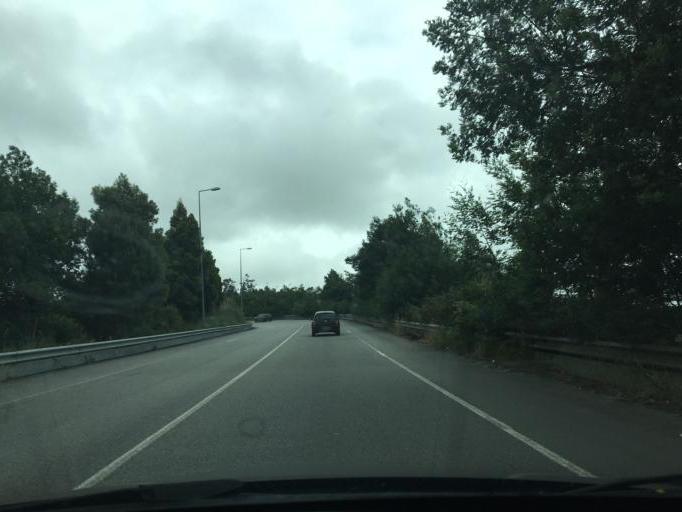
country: PT
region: Porto
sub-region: Matosinhos
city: Santa Cruz do Bispo
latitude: 41.2233
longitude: -8.6676
